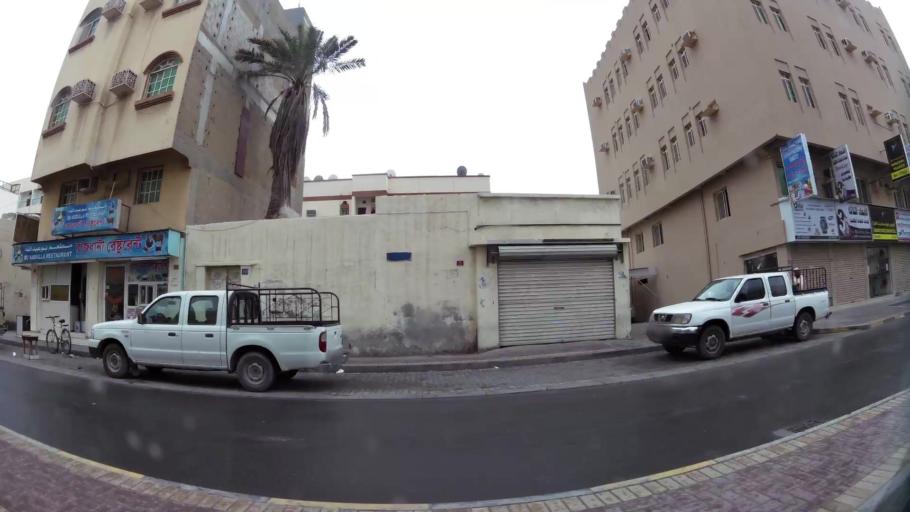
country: BH
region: Northern
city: Ar Rifa'
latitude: 26.1258
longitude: 50.5674
